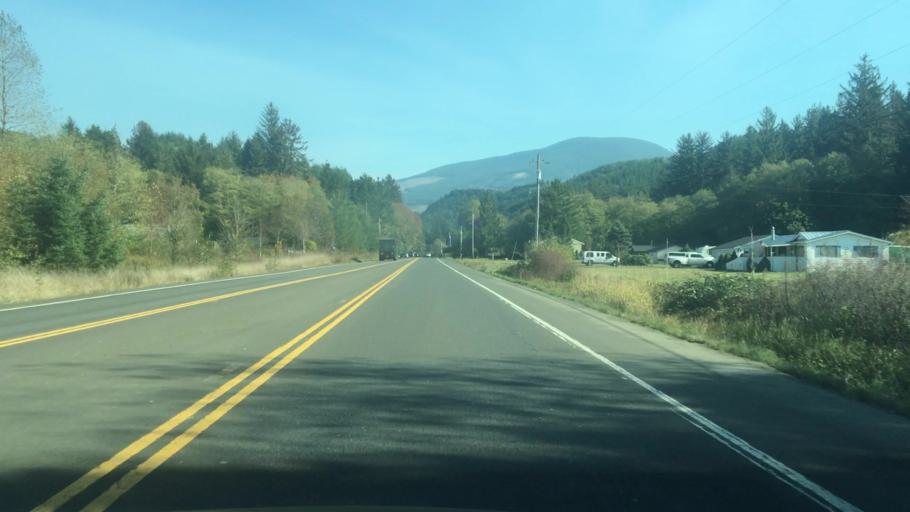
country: US
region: Oregon
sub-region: Lincoln County
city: Rose Lodge
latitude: 45.0213
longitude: -123.8570
